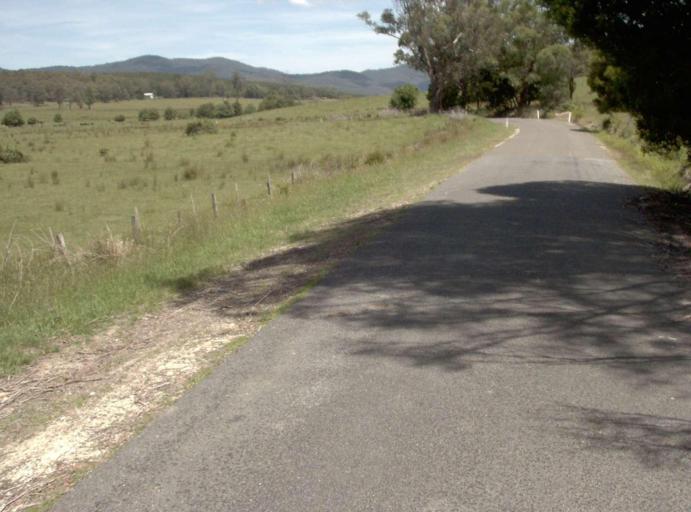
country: AU
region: New South Wales
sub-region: Bombala
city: Bombala
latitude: -37.3881
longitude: 149.0128
